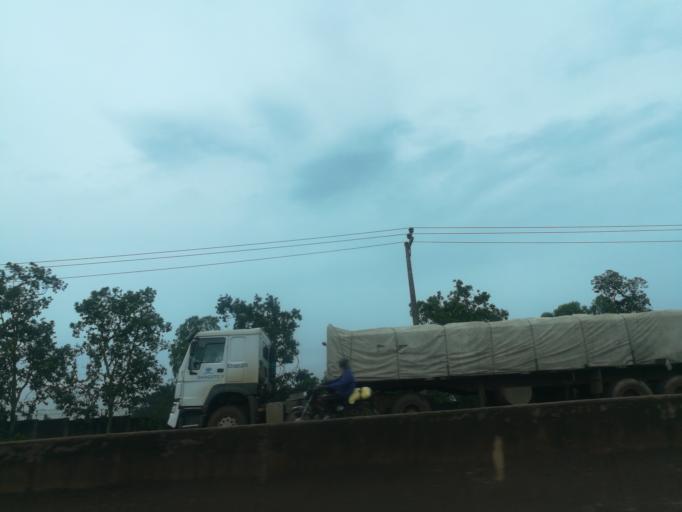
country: NG
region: Oyo
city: Ibadan
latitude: 7.3944
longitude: 3.9673
